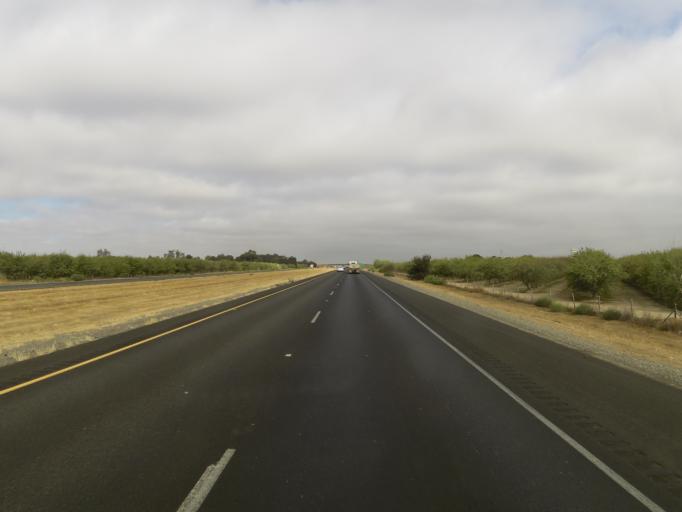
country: US
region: California
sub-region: Yolo County
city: Dunnigan
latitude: 38.9179
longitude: -121.9949
